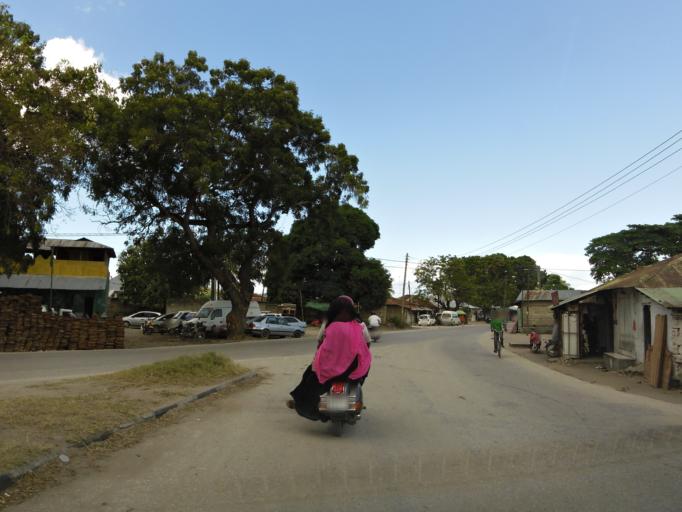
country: TZ
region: Zanzibar Urban/West
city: Zanzibar
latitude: -6.1641
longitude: 39.2074
